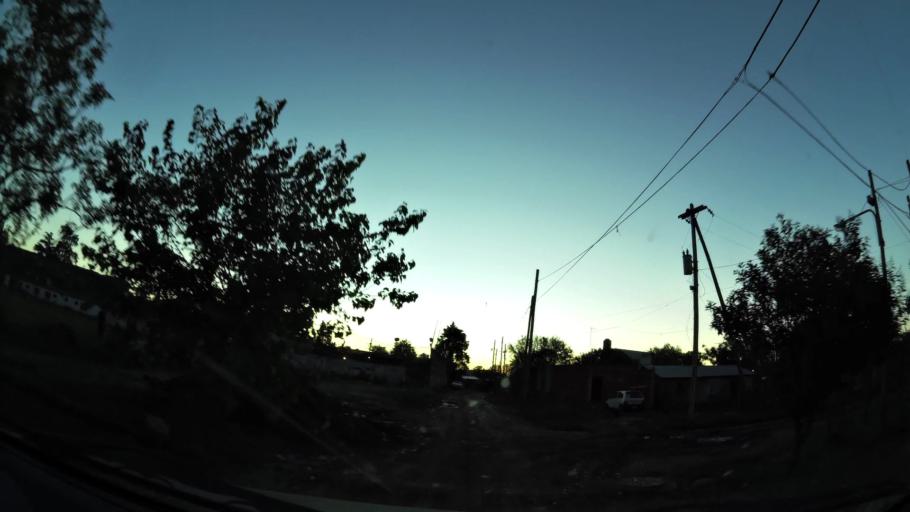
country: AR
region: Buenos Aires
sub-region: Partido de Almirante Brown
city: Adrogue
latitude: -34.7893
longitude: -58.3235
